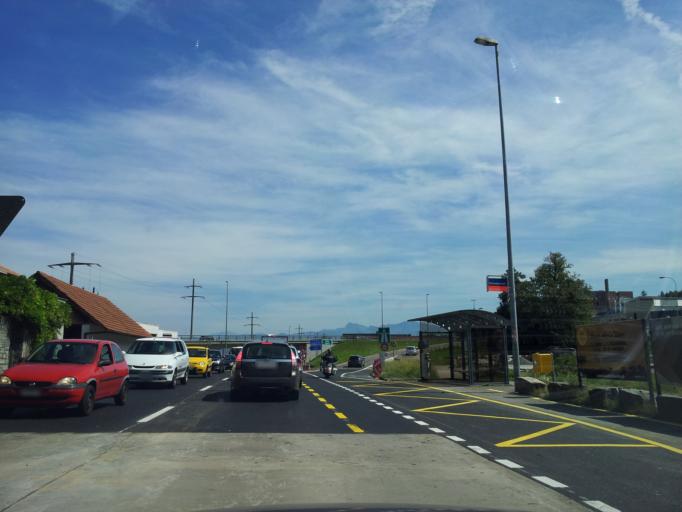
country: CH
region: Schwyz
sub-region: Bezirk Hoefe
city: Freienbach
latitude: 47.2020
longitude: 8.7908
